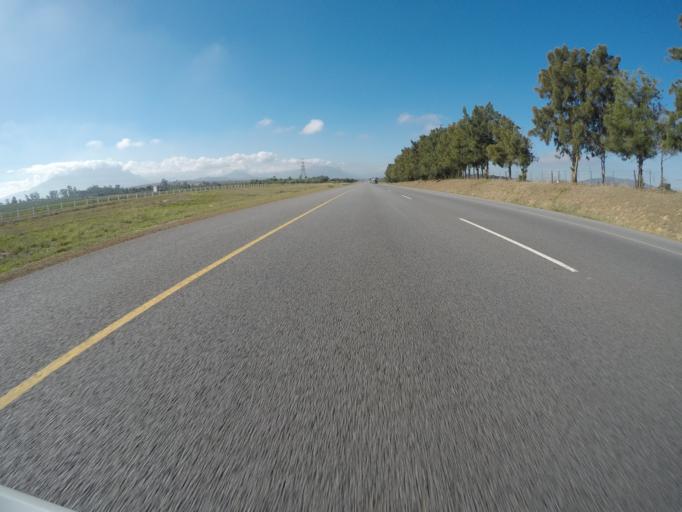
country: ZA
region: Western Cape
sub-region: City of Cape Town
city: Kraaifontein
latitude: -33.8480
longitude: 18.8041
